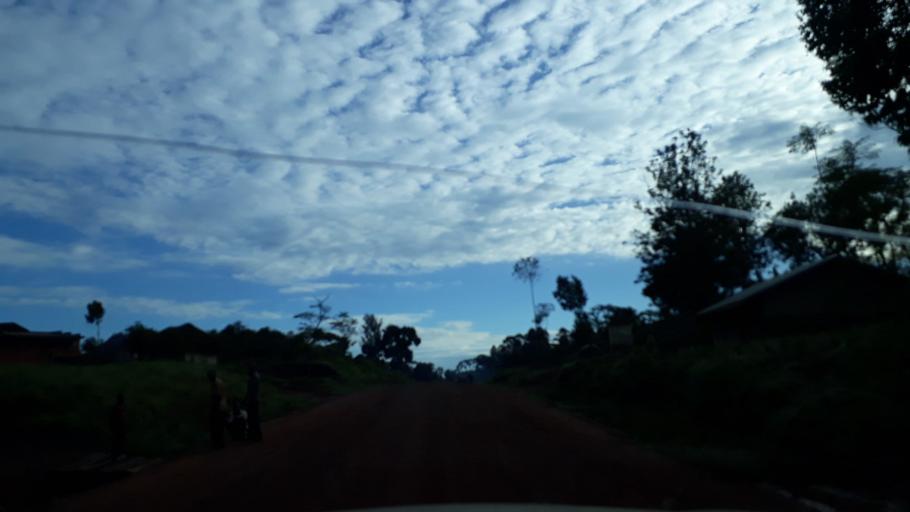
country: UG
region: Northern Region
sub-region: Zombo District
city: Paidha
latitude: 2.2331
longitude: 30.8586
